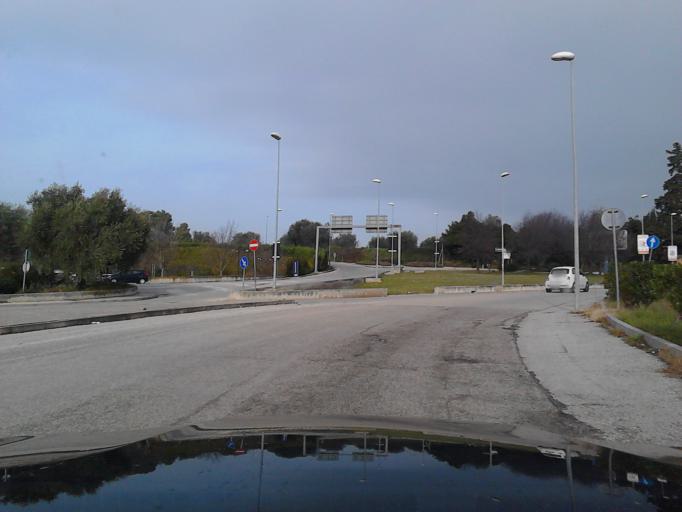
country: IT
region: Abruzzo
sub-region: Provincia di Teramo
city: Villa Rosa
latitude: 42.8359
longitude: 13.8945
